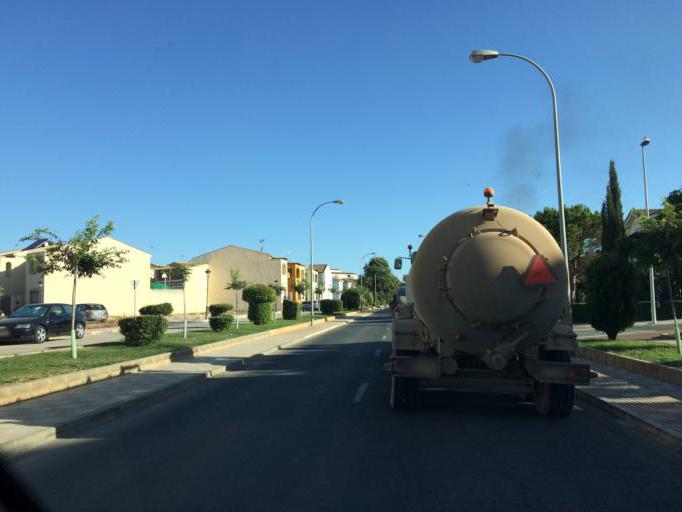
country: ES
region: Andalusia
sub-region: Provincia de Malaga
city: Campillos
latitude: 37.0420
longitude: -4.8598
